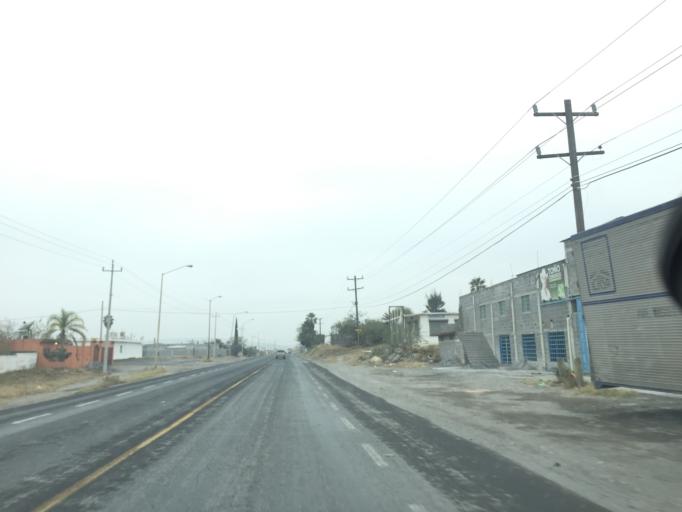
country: MX
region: Nuevo Leon
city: Mina
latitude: 26.0022
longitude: -100.5267
